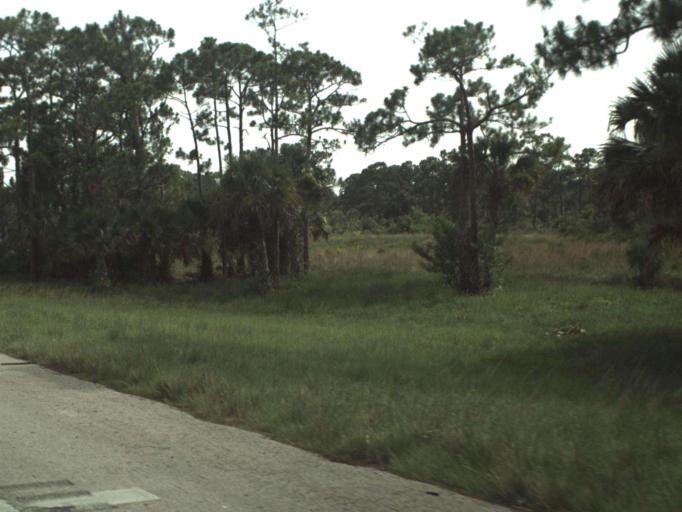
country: US
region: Florida
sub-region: Saint Lucie County
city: River Park
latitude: 27.3432
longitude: -80.4144
